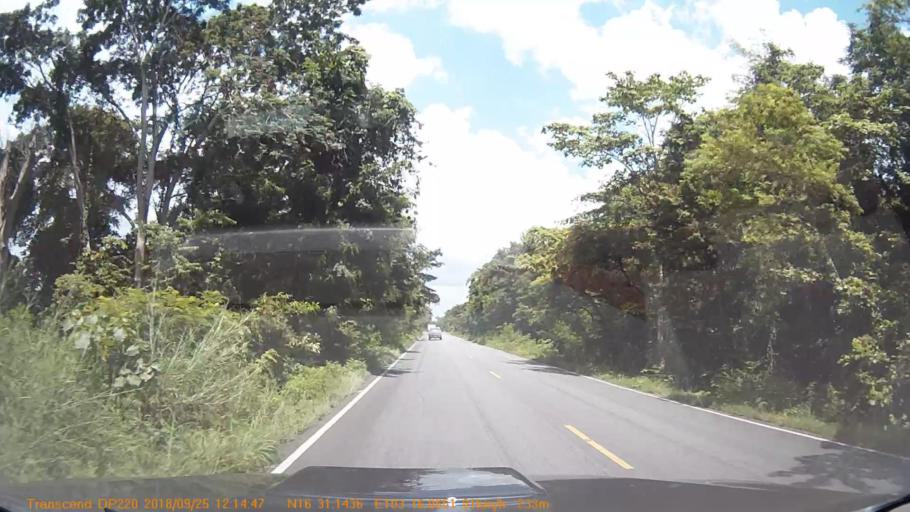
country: TH
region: Kalasin
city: Huai Mek
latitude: 16.5191
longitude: 103.2678
